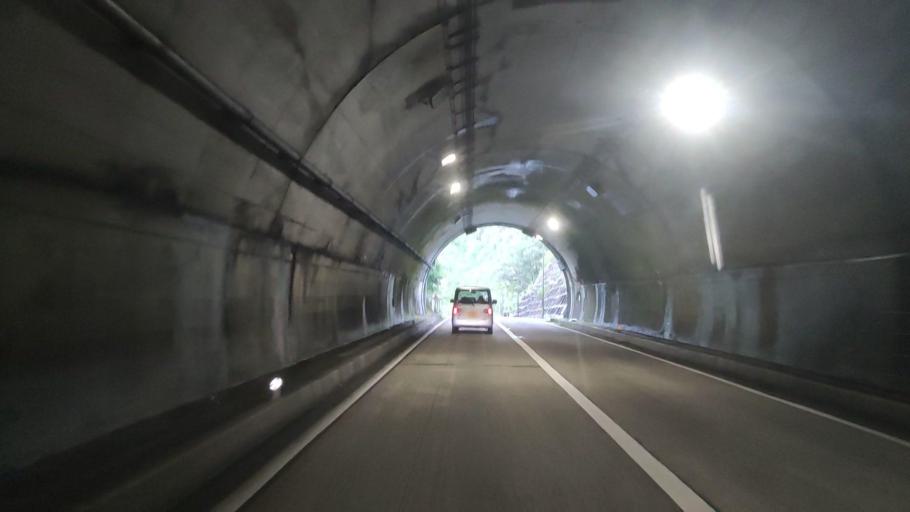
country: JP
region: Wakayama
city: Tanabe
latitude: 33.7809
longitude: 135.5049
